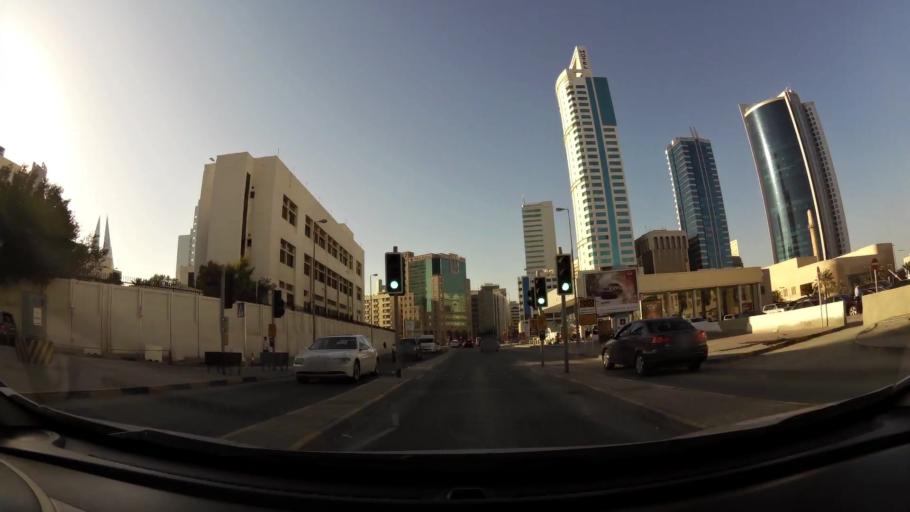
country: BH
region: Manama
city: Manama
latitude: 26.2382
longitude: 50.5910
